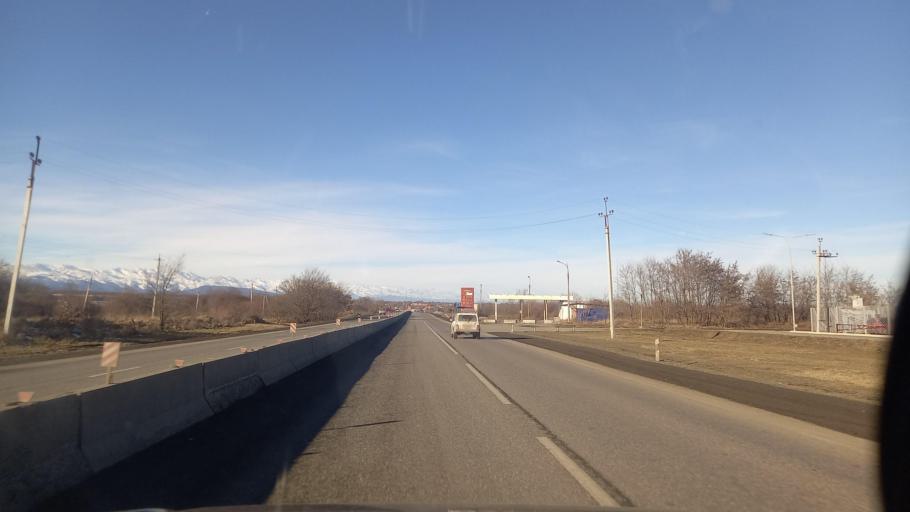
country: RU
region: North Ossetia
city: Gizel'
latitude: 43.0267
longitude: 44.6155
